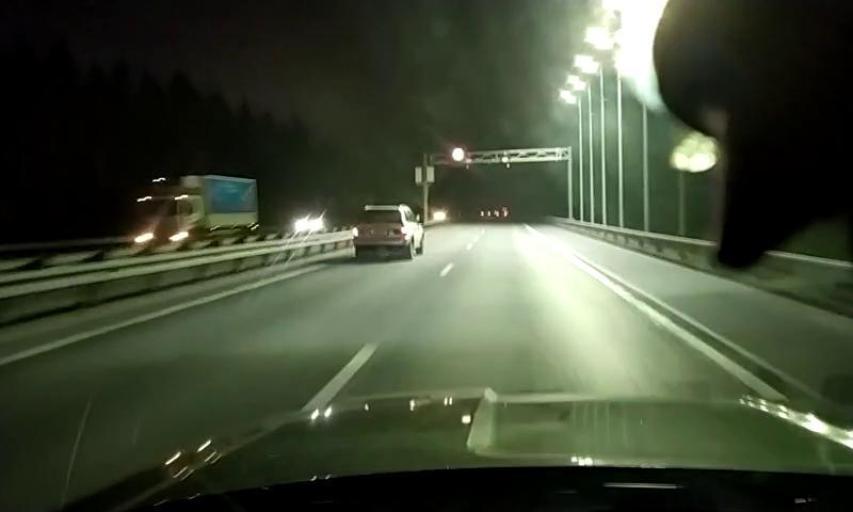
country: RU
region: Leningrad
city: Agalatovo
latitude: 60.2164
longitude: 30.3594
